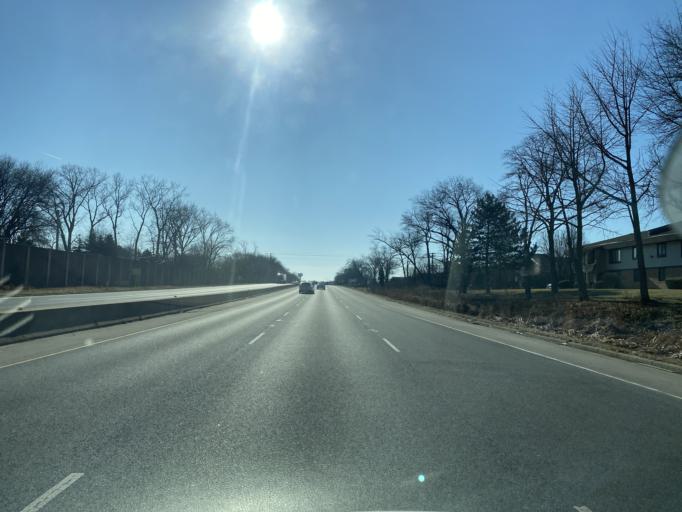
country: US
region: Illinois
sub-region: DuPage County
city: Clarendon Hills
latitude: 41.7827
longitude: -87.9469
